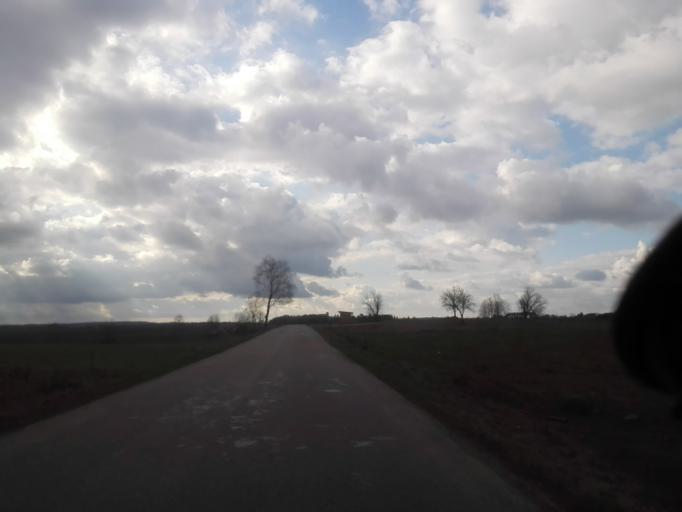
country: PL
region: Podlasie
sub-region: Suwalki
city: Suwalki
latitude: 54.2218
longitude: 22.8360
